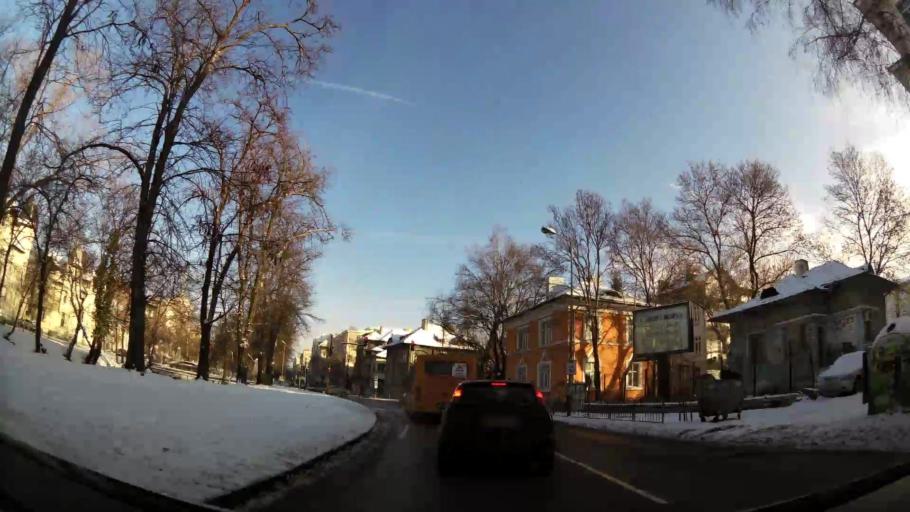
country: BG
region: Sofia-Capital
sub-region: Stolichna Obshtina
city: Sofia
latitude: 42.6935
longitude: 23.3464
